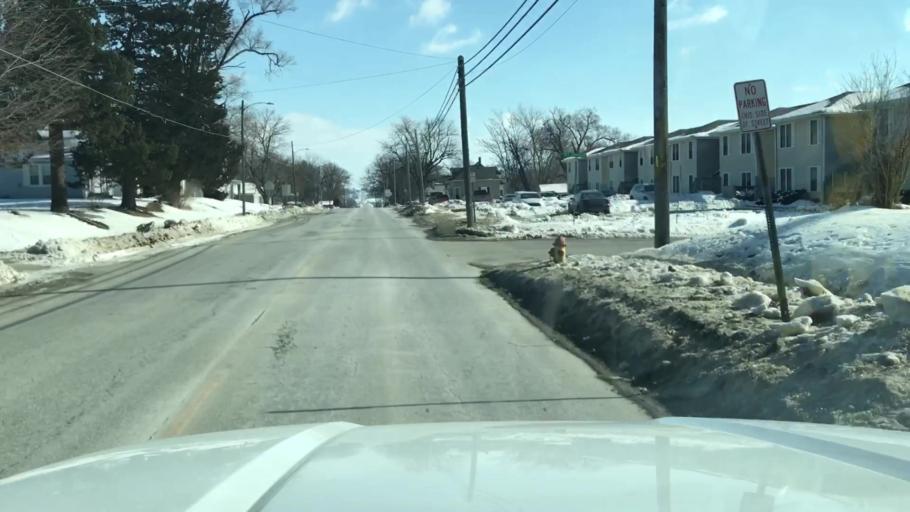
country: US
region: Missouri
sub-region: Nodaway County
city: Maryville
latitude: 40.3455
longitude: -94.8673
